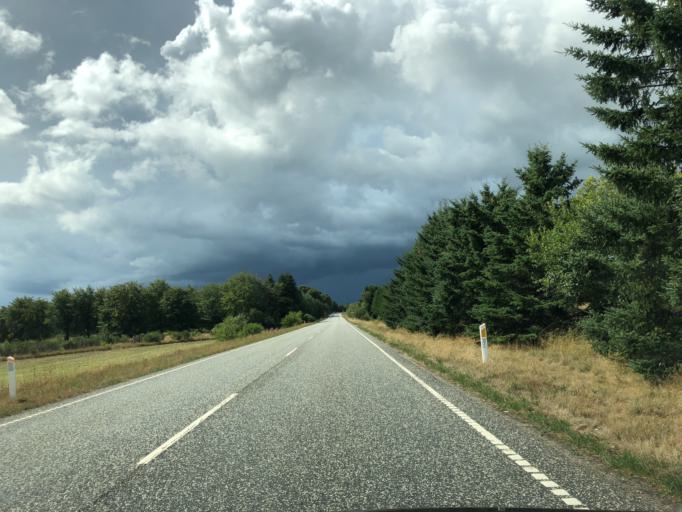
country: DK
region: Central Jutland
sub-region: Silkeborg Kommune
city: Silkeborg
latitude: 56.1430
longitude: 9.4338
